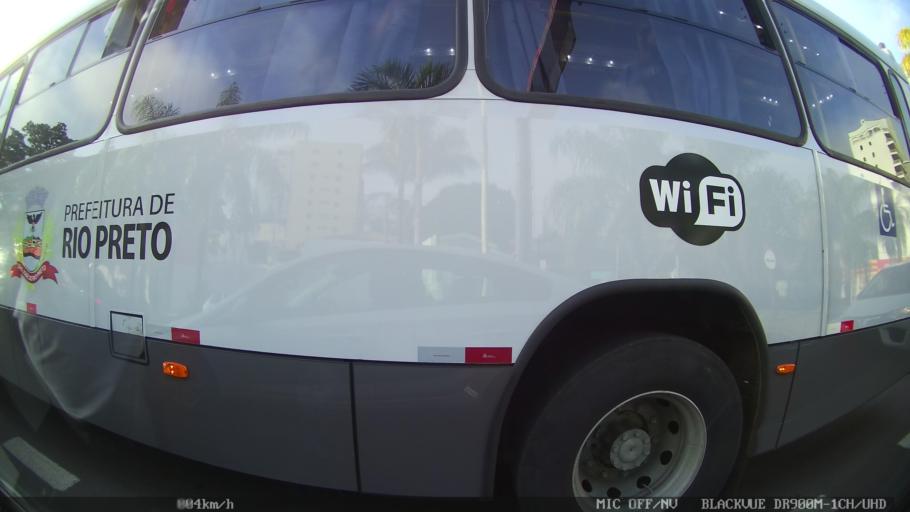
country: BR
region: Sao Paulo
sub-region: Sao Jose Do Rio Preto
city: Sao Jose do Rio Preto
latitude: -20.8185
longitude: -49.3821
